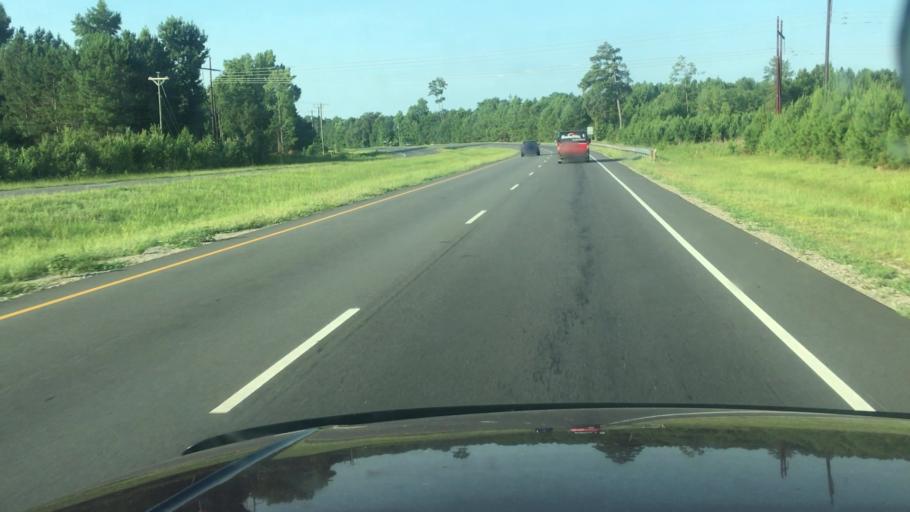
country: US
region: North Carolina
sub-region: Cumberland County
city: Vander
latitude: 34.9470
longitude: -78.8463
